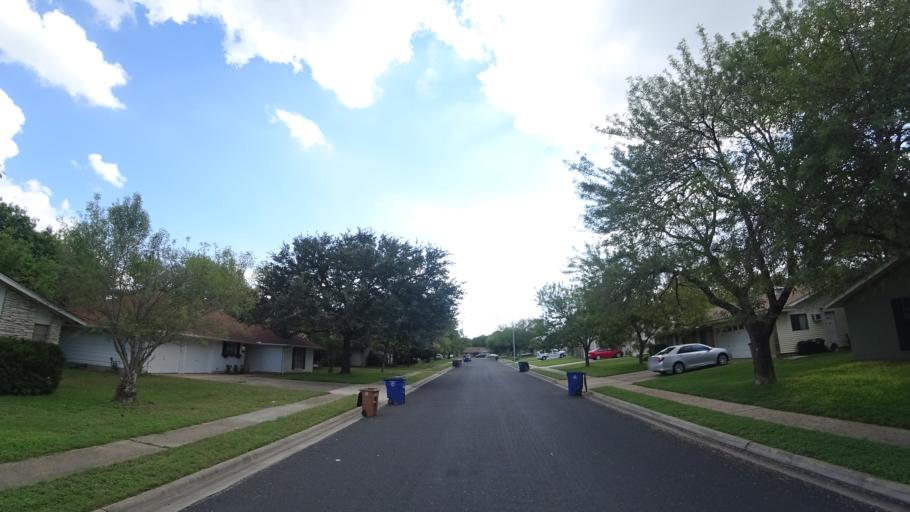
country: US
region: Texas
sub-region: Travis County
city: Wells Branch
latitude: 30.3622
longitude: -97.7142
